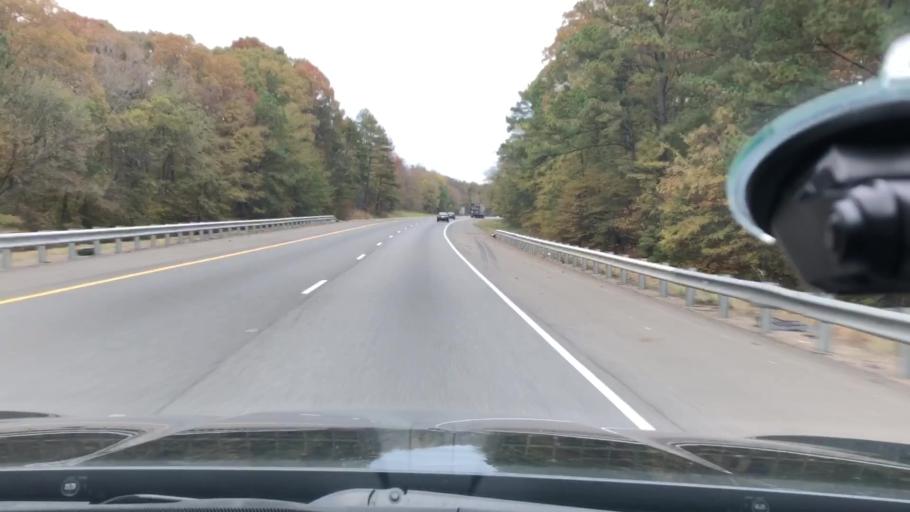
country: US
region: Arkansas
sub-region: Hot Spring County
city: Malvern
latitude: 34.3544
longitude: -92.8847
